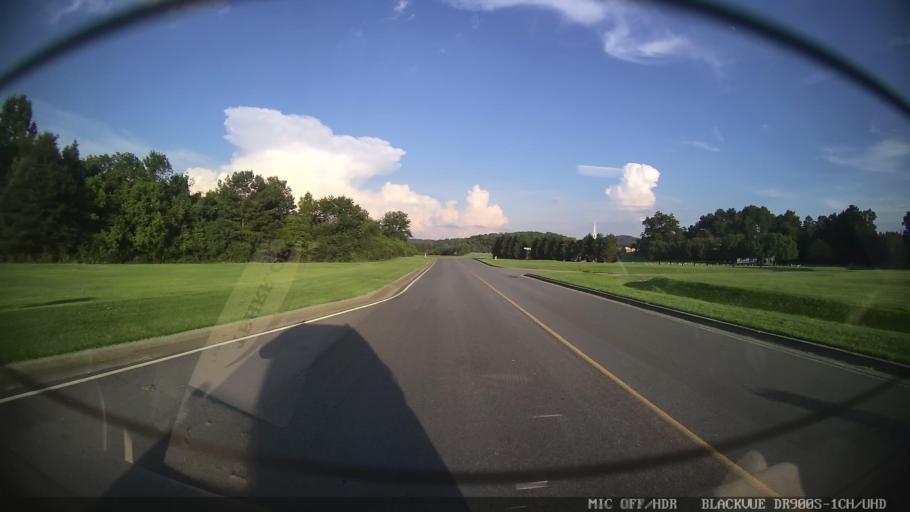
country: US
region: Georgia
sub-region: Bartow County
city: Cartersville
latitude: 34.2181
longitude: -84.7910
